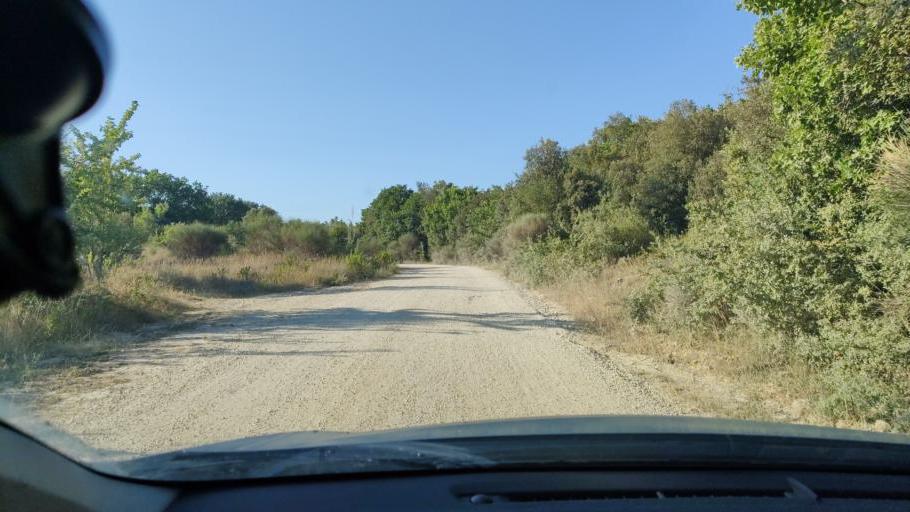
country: IT
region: Umbria
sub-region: Provincia di Terni
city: Amelia
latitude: 42.5376
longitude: 12.3793
